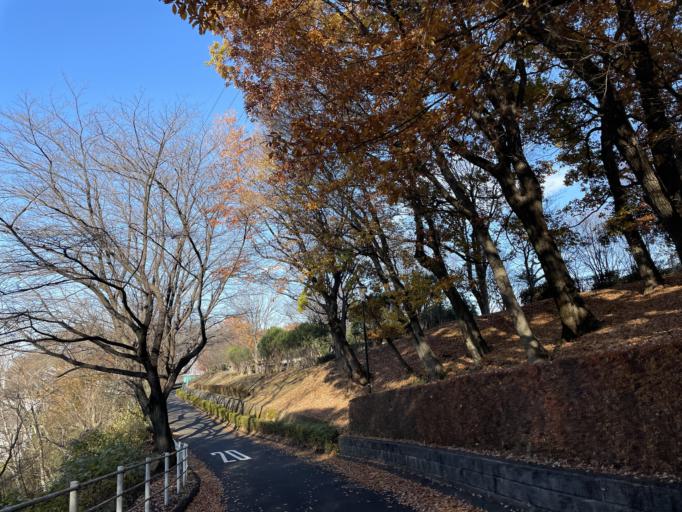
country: JP
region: Saitama
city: Asaka
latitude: 35.7810
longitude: 139.5790
